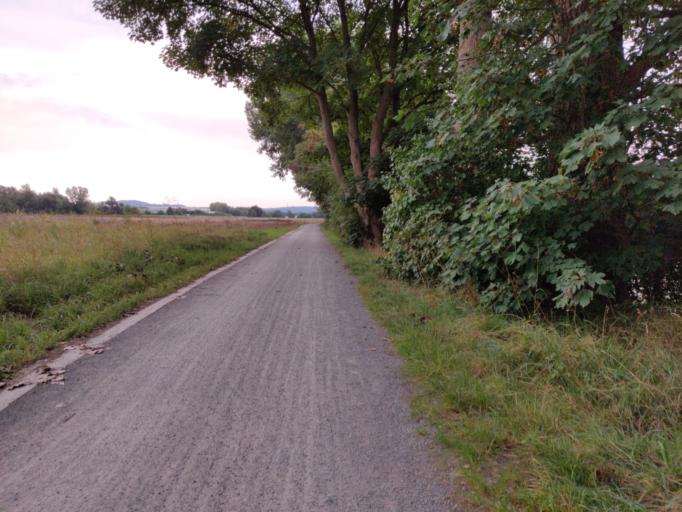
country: DE
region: Lower Saxony
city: Hameln
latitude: 52.0890
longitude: 9.3641
